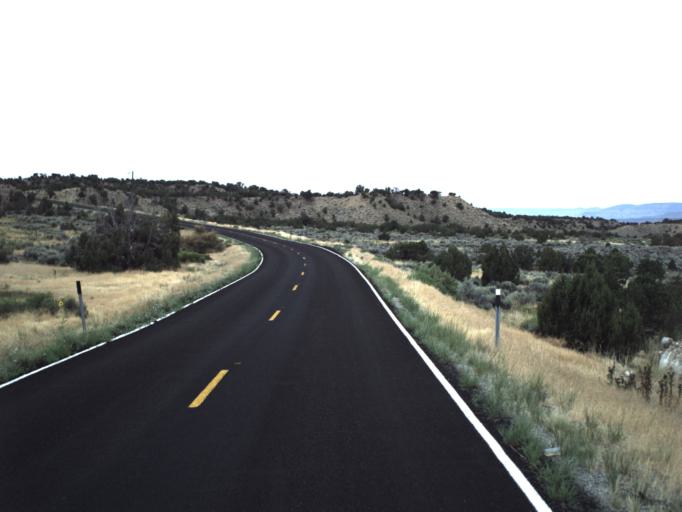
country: US
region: Utah
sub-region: Carbon County
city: East Carbon City
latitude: 39.4908
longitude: -110.4040
